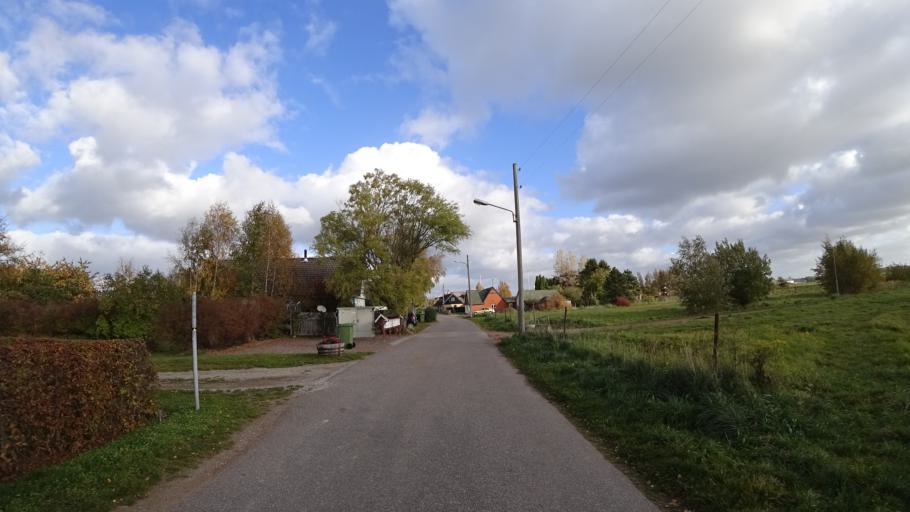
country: SE
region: Skane
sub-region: Staffanstorps Kommun
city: Staffanstorp
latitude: 55.6275
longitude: 13.2149
